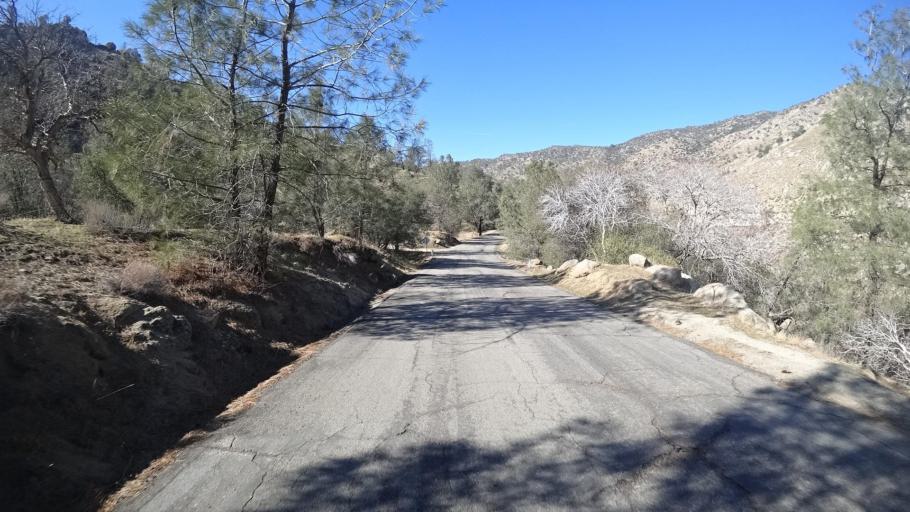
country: US
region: California
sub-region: Kern County
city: Bodfish
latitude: 35.5658
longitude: -118.5736
